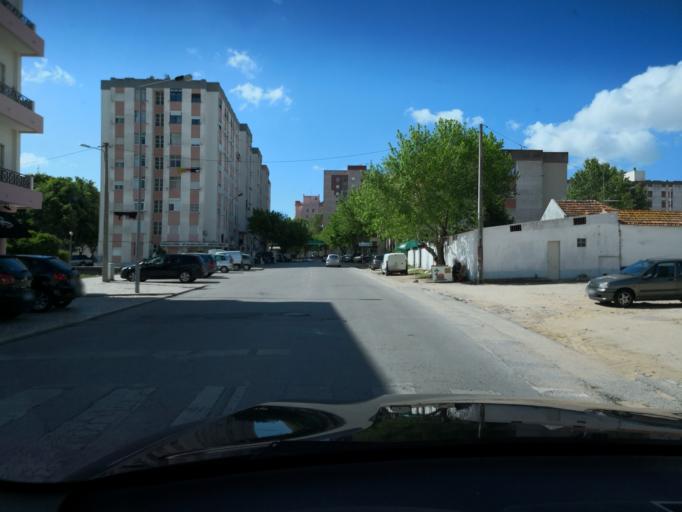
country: PT
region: Setubal
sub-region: Setubal
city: Setubal
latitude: 38.5274
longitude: -8.8703
